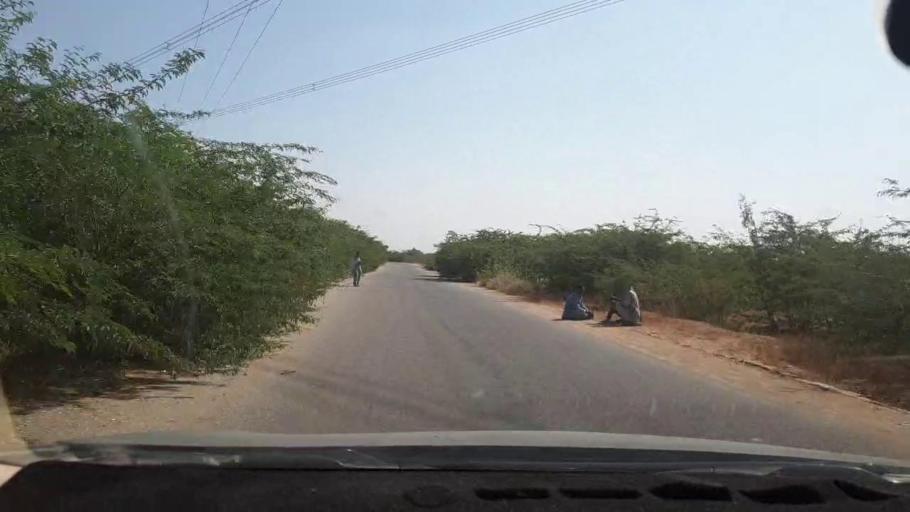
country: PK
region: Sindh
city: Malir Cantonment
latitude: 25.1431
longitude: 67.1934
